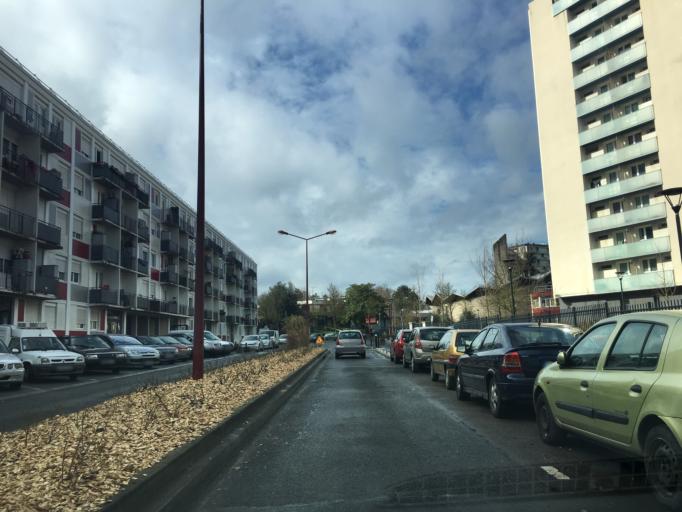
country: FR
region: Ile-de-France
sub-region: Departement du Val-d'Oise
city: Arnouville
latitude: 49.0010
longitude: 2.4246
